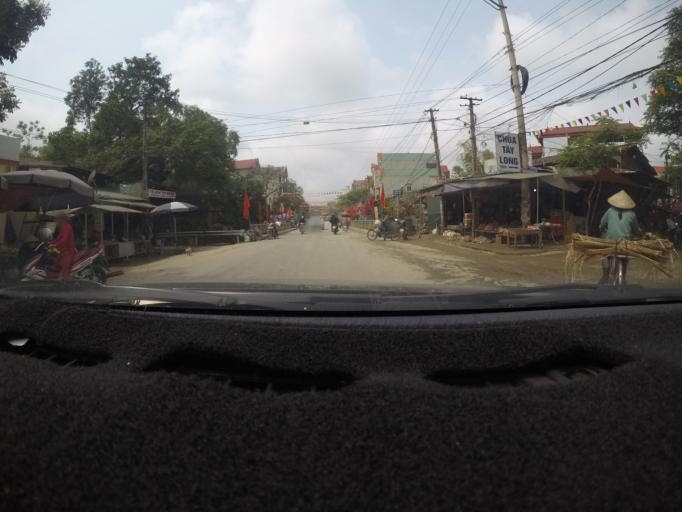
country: VN
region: Phu Tho
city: Doan Hung
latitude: 21.6320
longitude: 105.1310
